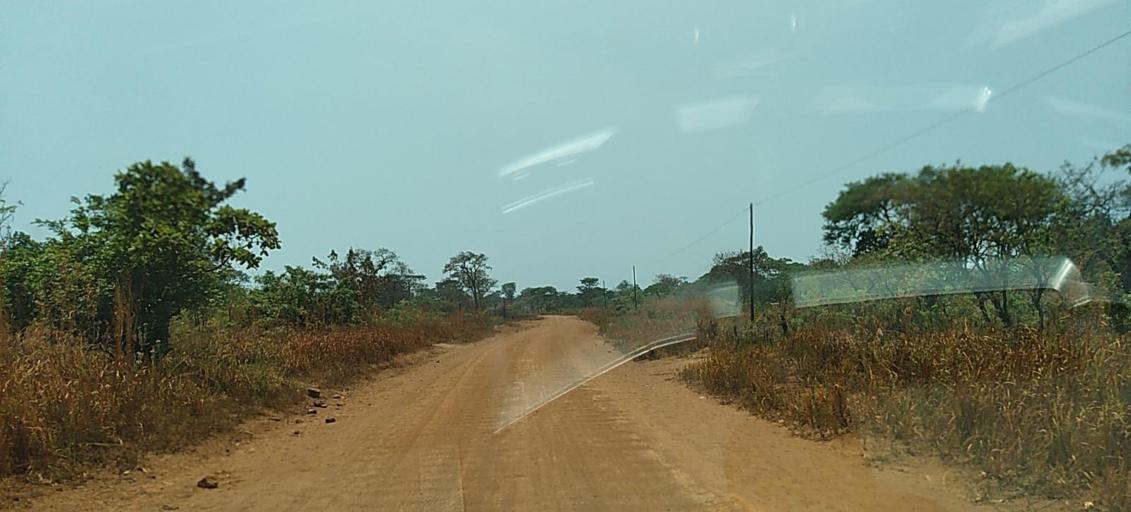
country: CD
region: Katanga
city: Kipushi
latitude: -11.9356
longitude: 26.9644
